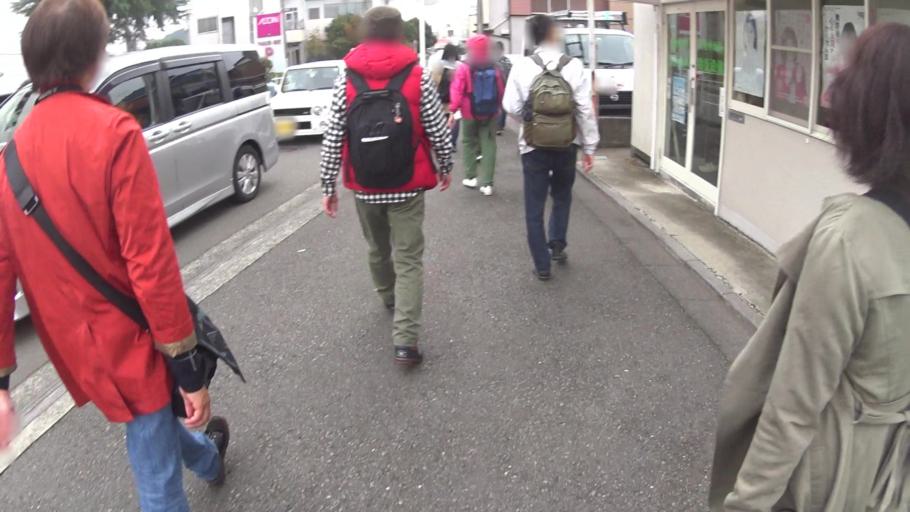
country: JP
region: Kanagawa
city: Hadano
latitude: 35.3776
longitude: 139.2268
